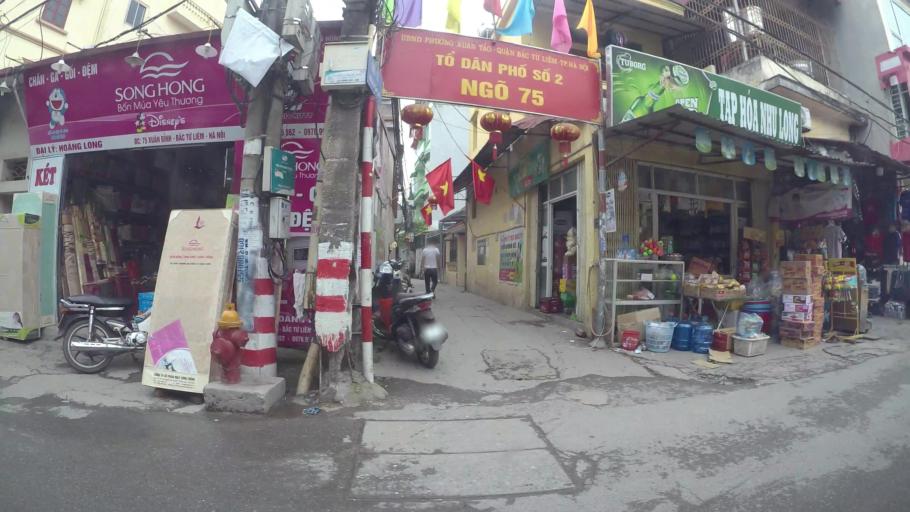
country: VN
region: Ha Noi
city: Tay Ho
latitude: 21.0706
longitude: 105.8010
